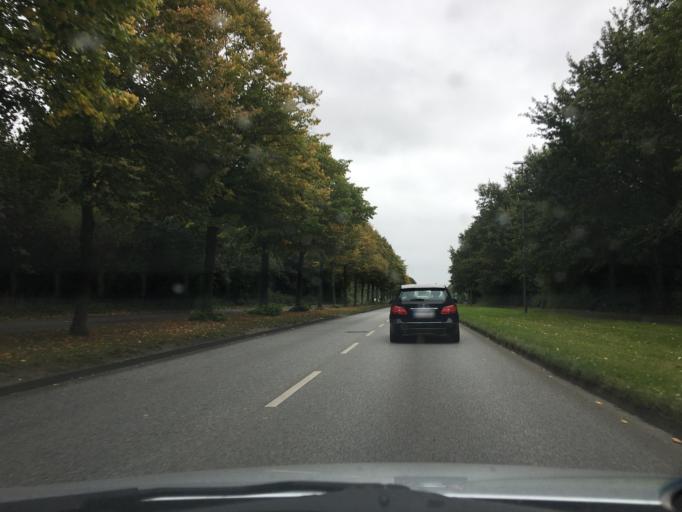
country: DE
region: Schleswig-Holstein
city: Kronshagen
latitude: 54.3258
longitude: 10.0597
